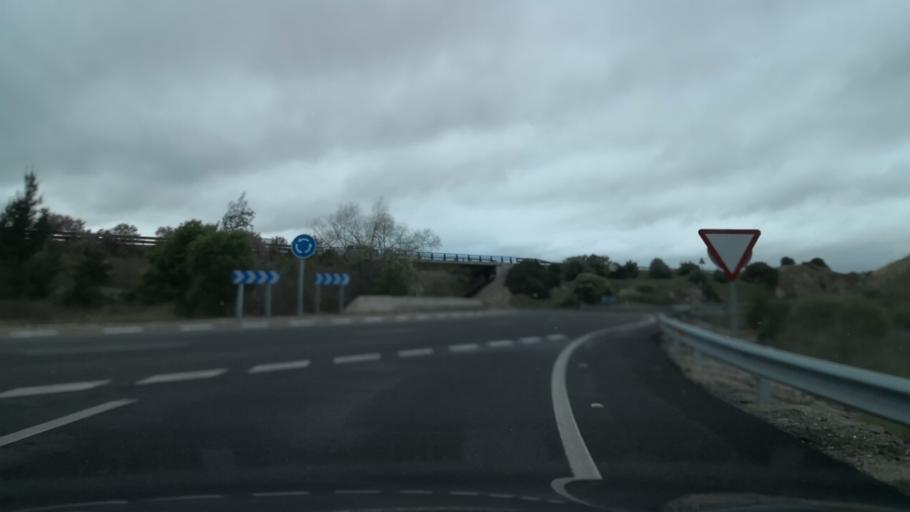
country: ES
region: Extremadura
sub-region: Provincia de Caceres
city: Caceres
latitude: 39.4623
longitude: -6.4207
